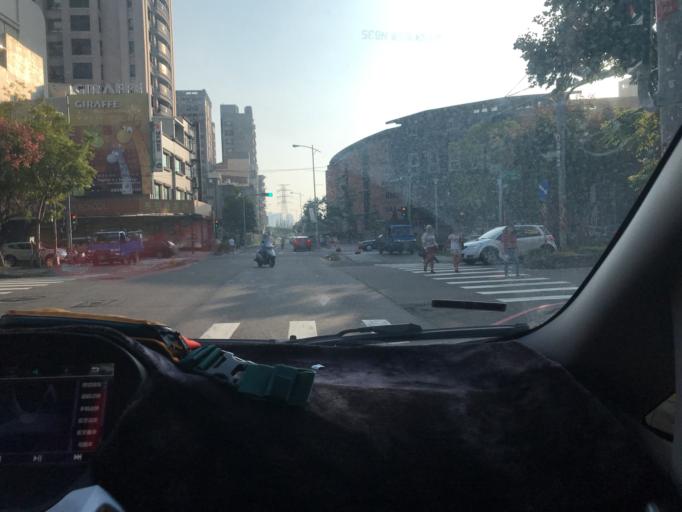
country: TW
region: Taiwan
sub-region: Hsinchu
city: Zhubei
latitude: 24.8055
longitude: 121.0339
